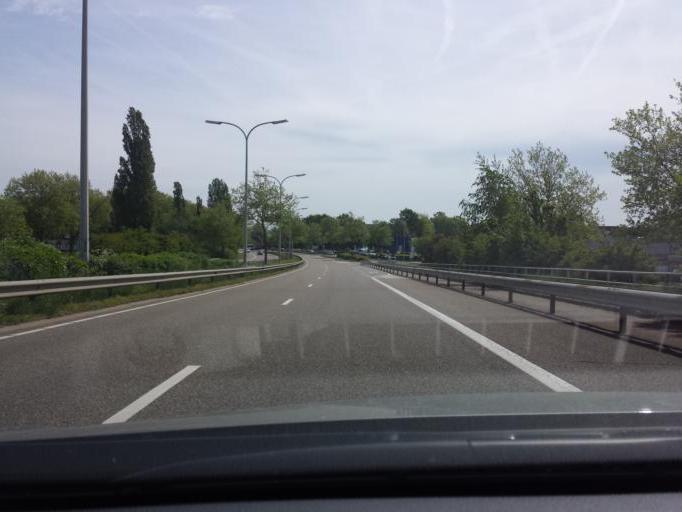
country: BE
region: Flanders
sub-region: Provincie Limburg
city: Hasselt
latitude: 50.9142
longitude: 5.3369
